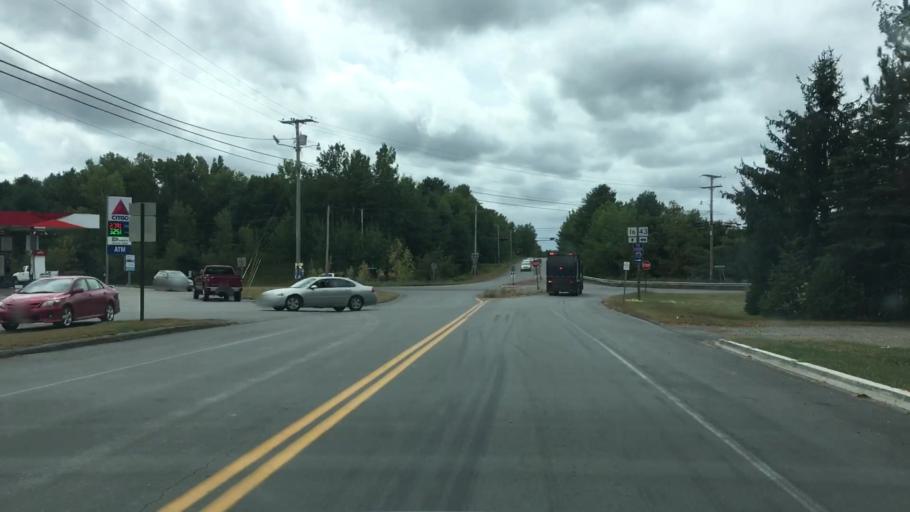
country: US
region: Maine
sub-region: Penobscot County
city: Milford
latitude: 44.9534
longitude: -68.6987
